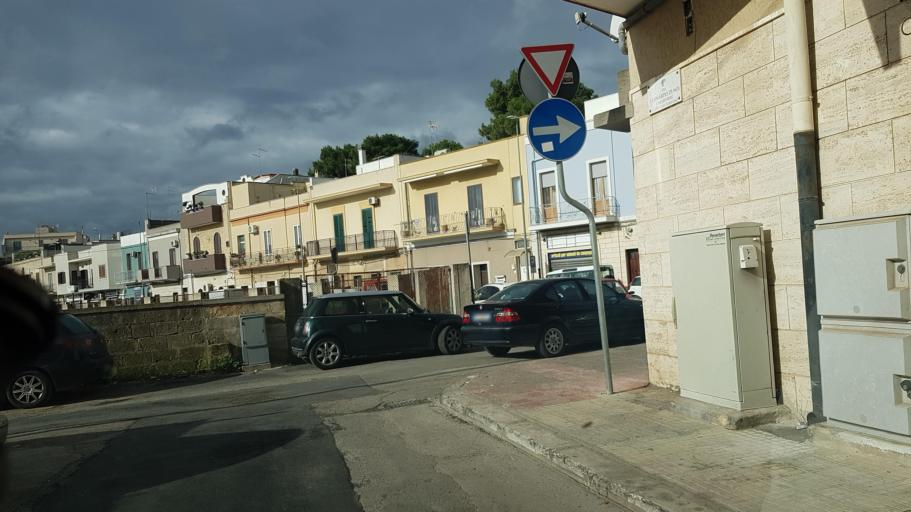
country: IT
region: Apulia
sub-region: Provincia di Brindisi
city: Francavilla Fontana
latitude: 40.5241
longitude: 17.5839
